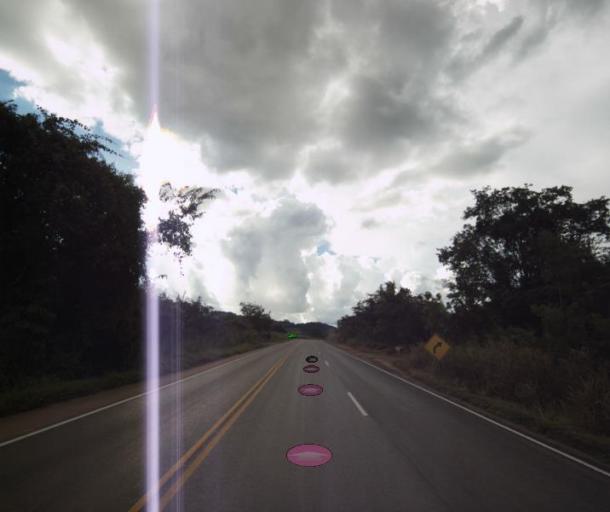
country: BR
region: Goias
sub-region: Rialma
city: Rialma
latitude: -15.2529
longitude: -49.5532
